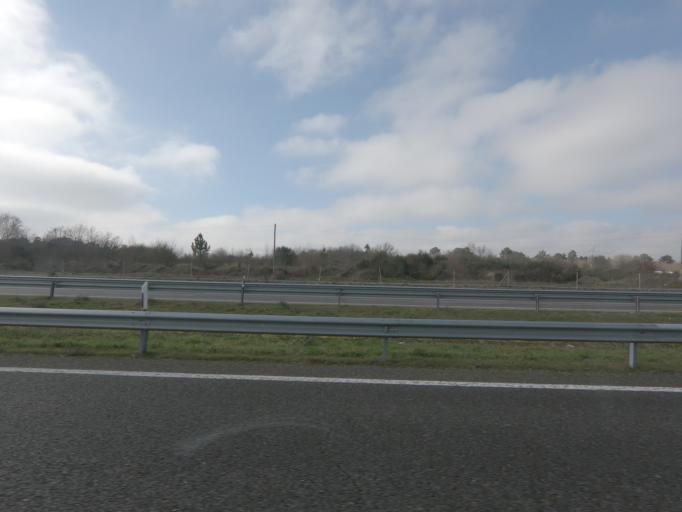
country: ES
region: Galicia
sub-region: Provincia de Ourense
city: Taboadela
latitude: 42.2599
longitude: -7.8683
